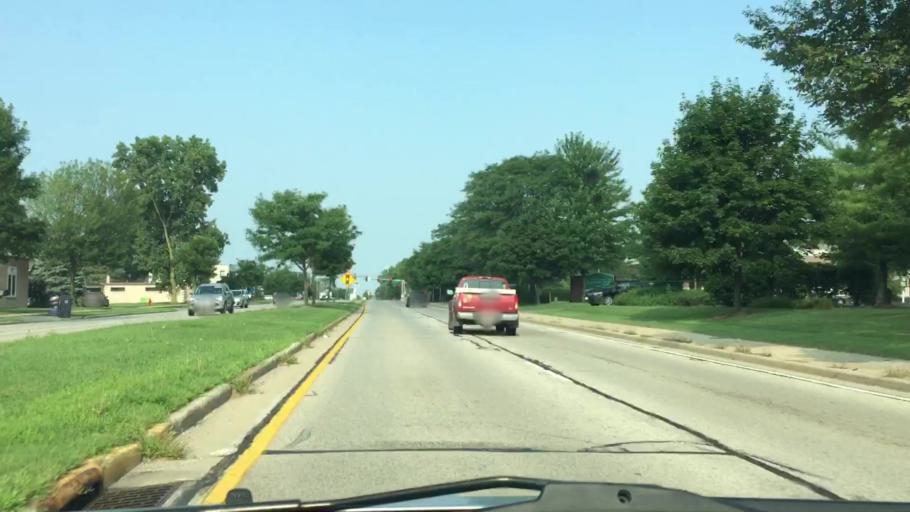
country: US
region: Wisconsin
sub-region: Waukesha County
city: Elm Grove
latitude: 43.0166
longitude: -88.0839
